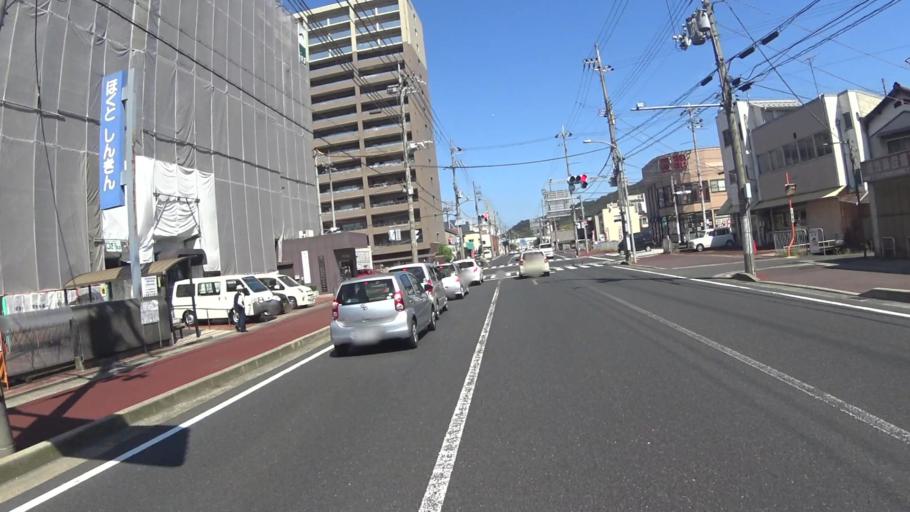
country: JP
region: Kyoto
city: Maizuru
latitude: 35.4447
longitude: 135.3285
